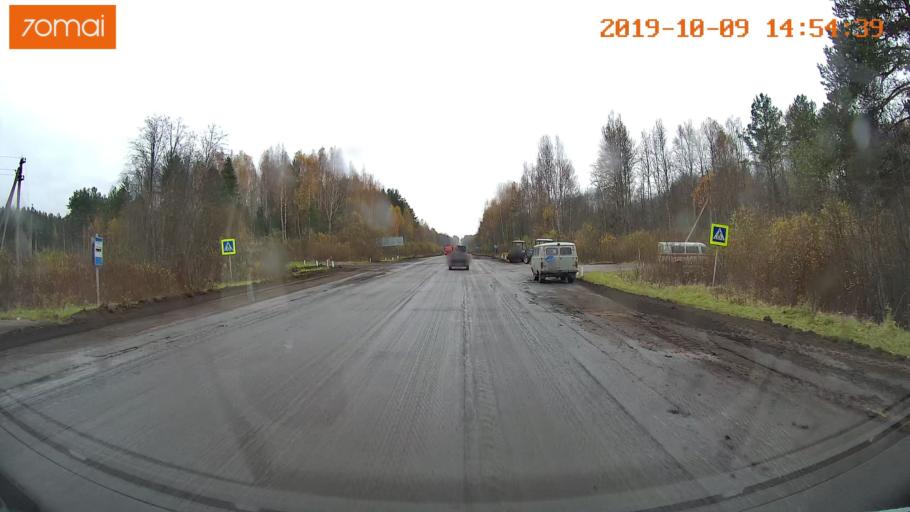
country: RU
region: Kostroma
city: Chistyye Bory
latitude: 58.3551
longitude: 41.6435
